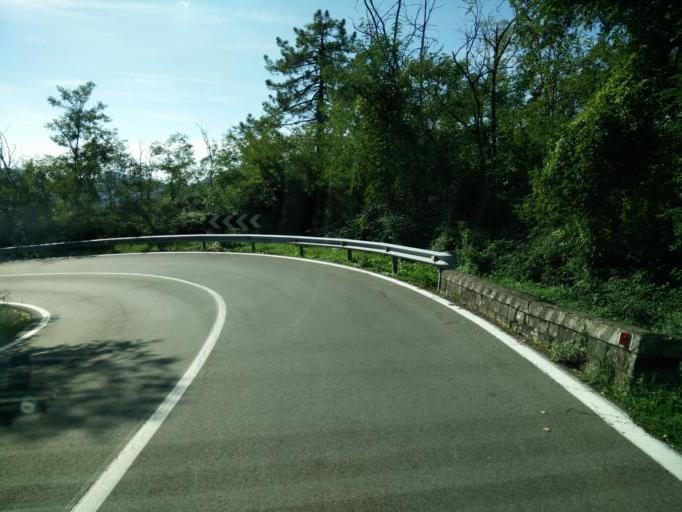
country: IT
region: Liguria
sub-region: Provincia di La Spezia
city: Carrodano
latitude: 44.2455
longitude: 9.6308
